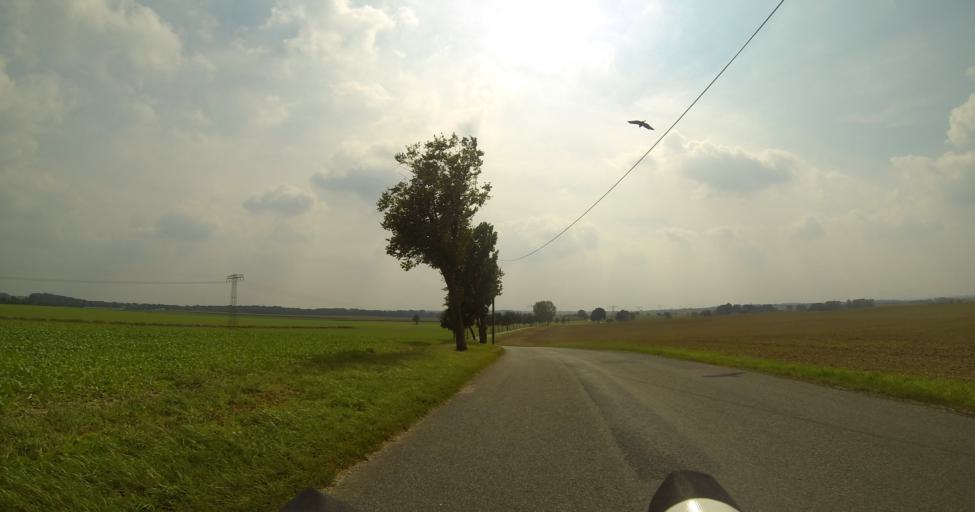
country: DE
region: Saxony
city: Ebersbach
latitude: 51.2367
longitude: 13.5937
